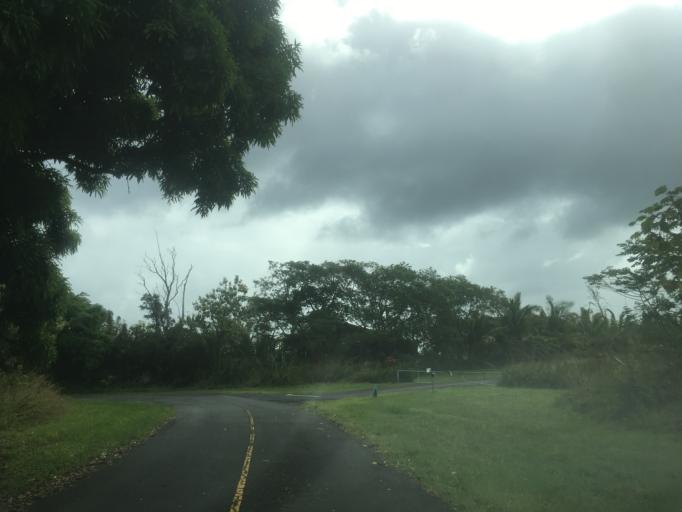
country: US
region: Hawaii
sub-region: Hawaii County
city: Leilani Estates
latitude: 19.4688
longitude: -154.8668
